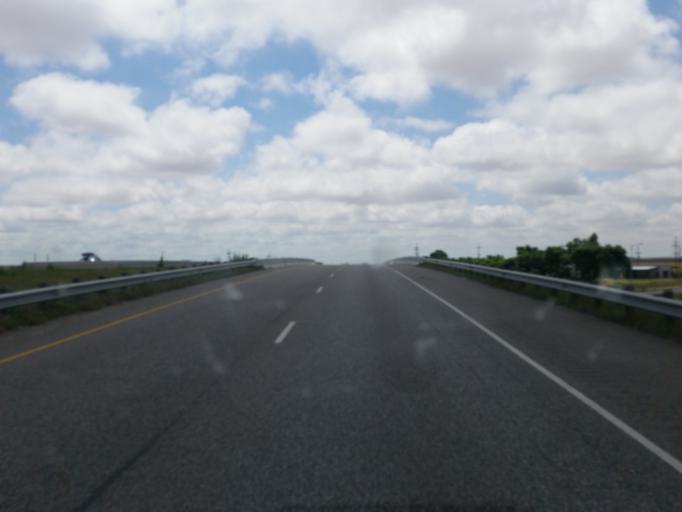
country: US
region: Texas
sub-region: Lubbock County
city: Slaton
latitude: 33.4203
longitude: -101.6436
